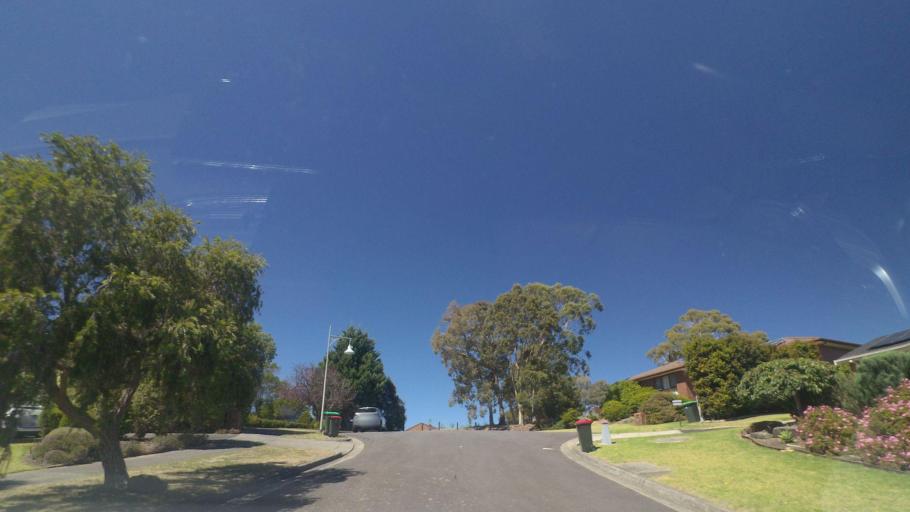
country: AU
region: Victoria
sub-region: Manningham
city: Donvale
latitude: -37.7699
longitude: 145.1782
